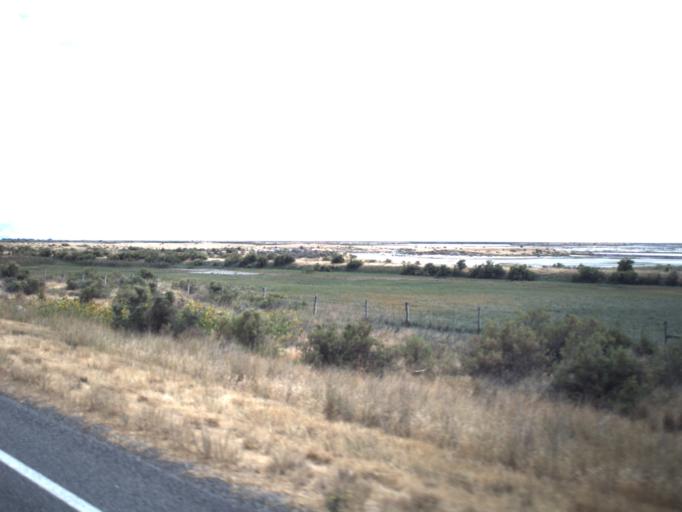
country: US
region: Utah
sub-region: Box Elder County
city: Elwood
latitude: 41.5816
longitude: -112.2565
